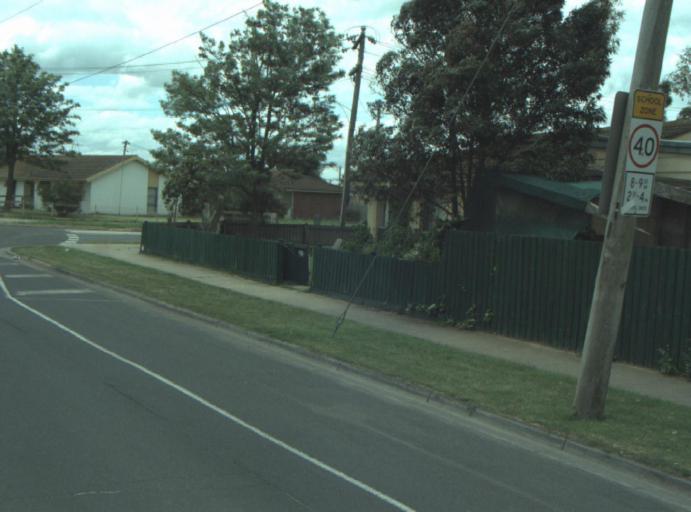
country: AU
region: Victoria
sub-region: Greater Geelong
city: Bell Park
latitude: -38.0658
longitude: 144.3677
